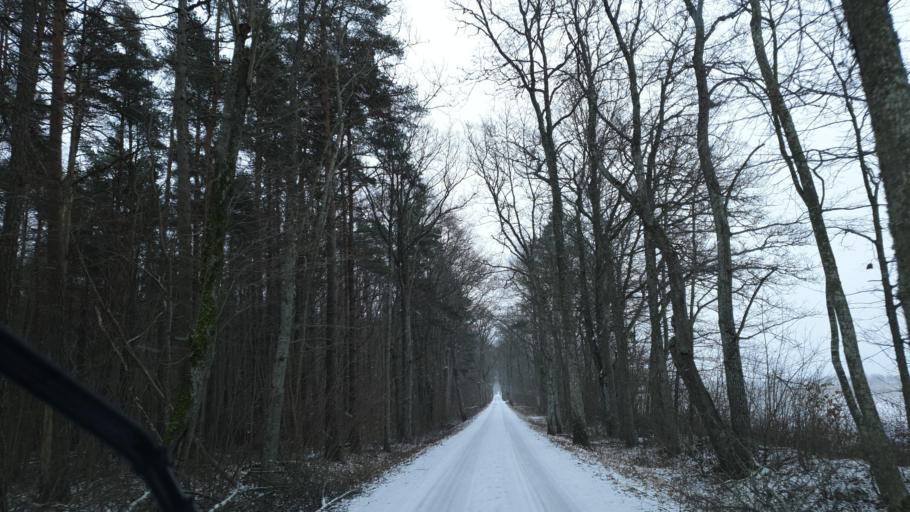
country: SE
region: Gotland
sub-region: Gotland
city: Visby
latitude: 57.5233
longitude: 18.4491
